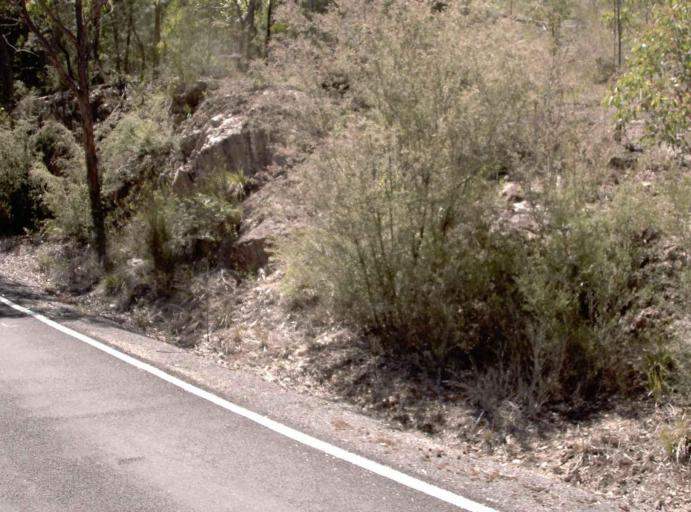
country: AU
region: Victoria
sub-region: East Gippsland
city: Lakes Entrance
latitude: -37.3726
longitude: 148.2194
